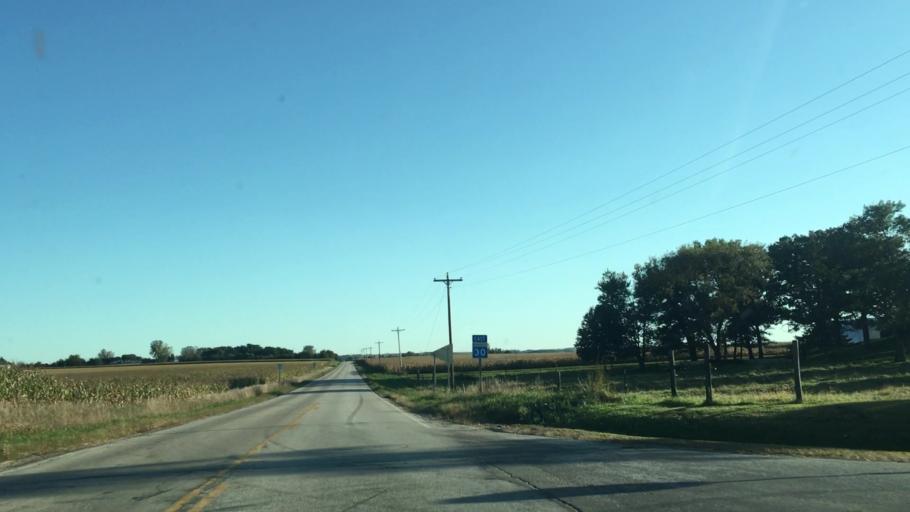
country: US
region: Minnesota
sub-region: Fillmore County
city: Chatfield
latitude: 43.8326
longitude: -92.0694
